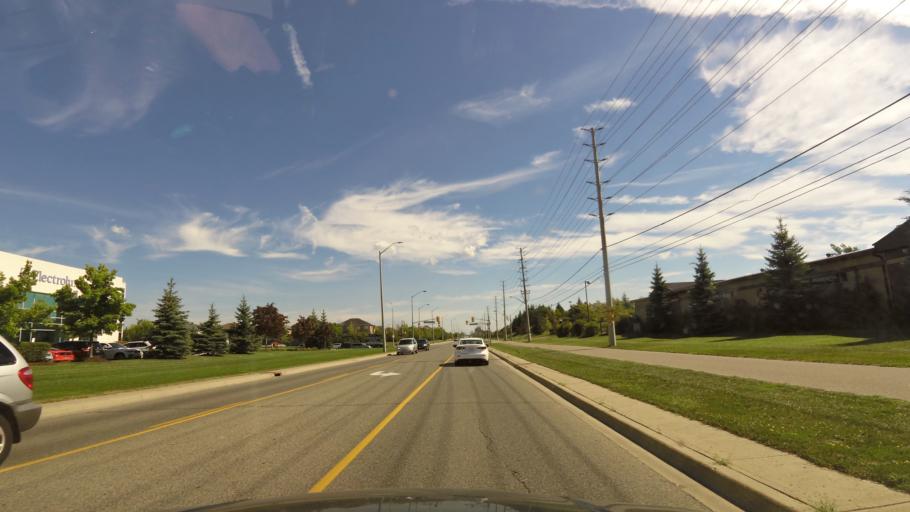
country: CA
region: Ontario
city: Mississauga
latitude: 43.6041
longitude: -79.6968
